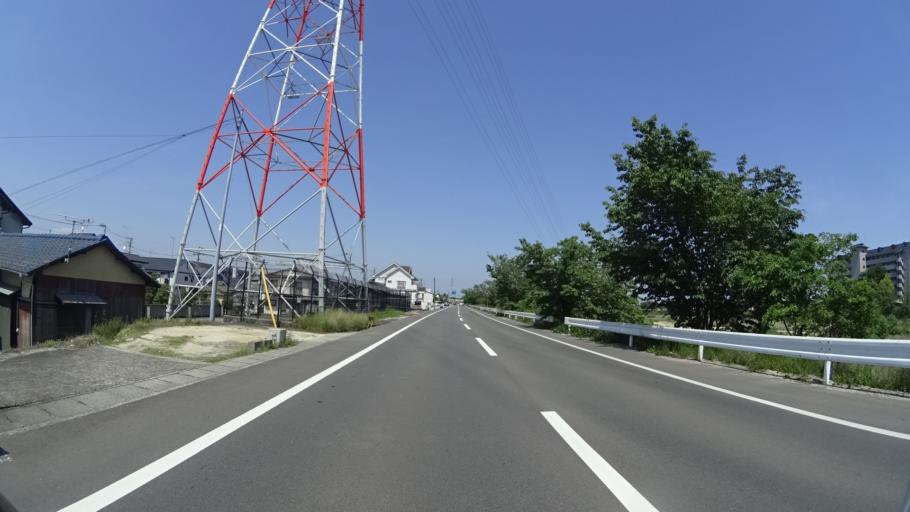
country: JP
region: Ehime
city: Hojo
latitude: 34.0441
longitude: 132.9824
